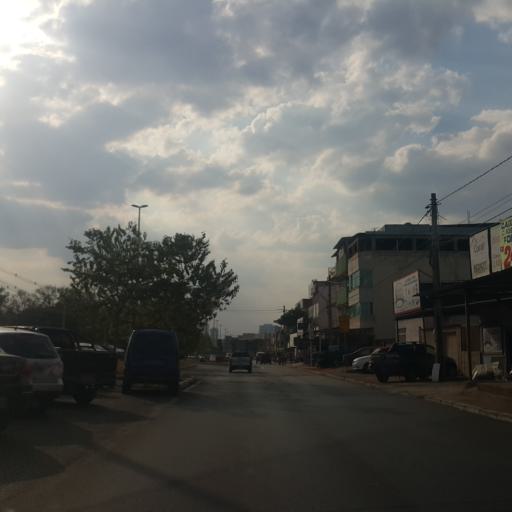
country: BR
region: Federal District
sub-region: Brasilia
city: Brasilia
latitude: -15.8618
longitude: -48.0259
